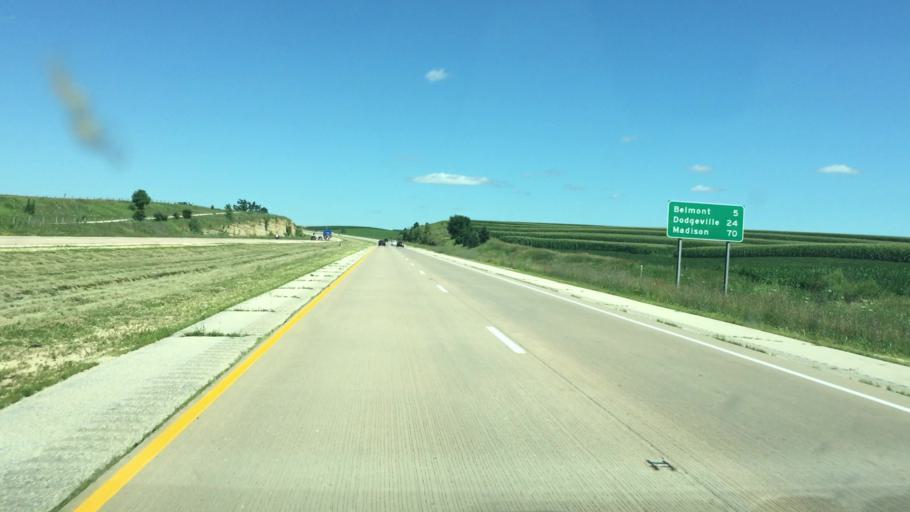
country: US
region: Wisconsin
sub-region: Grant County
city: Platteville
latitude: 42.7373
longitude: -90.4180
